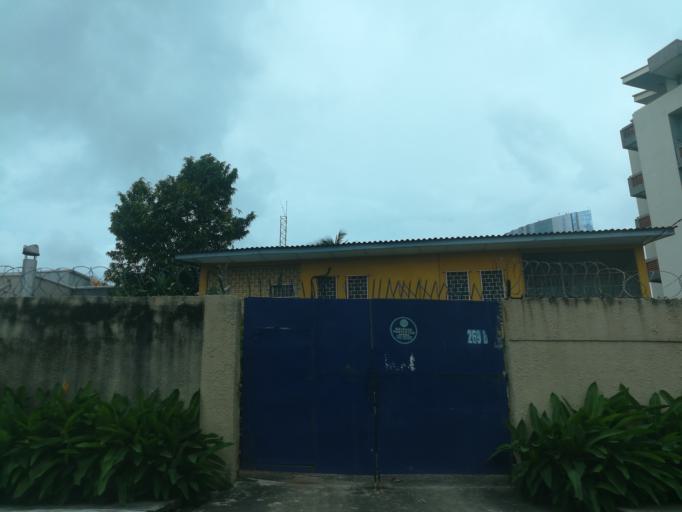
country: NG
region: Lagos
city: Ikoyi
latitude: 6.4323
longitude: 3.4224
